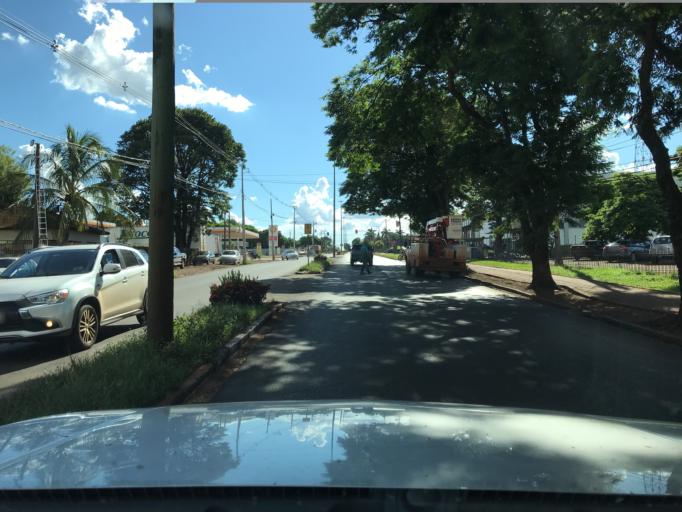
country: BR
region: Parana
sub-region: Palotina
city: Palotina
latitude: -24.2802
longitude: -53.8290
